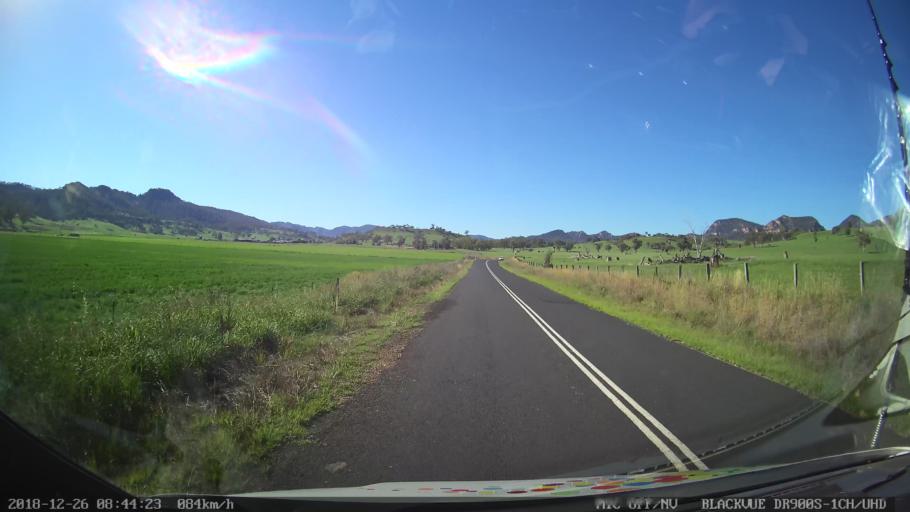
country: AU
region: New South Wales
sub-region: Mid-Western Regional
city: Kandos
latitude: -32.5138
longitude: 150.0810
